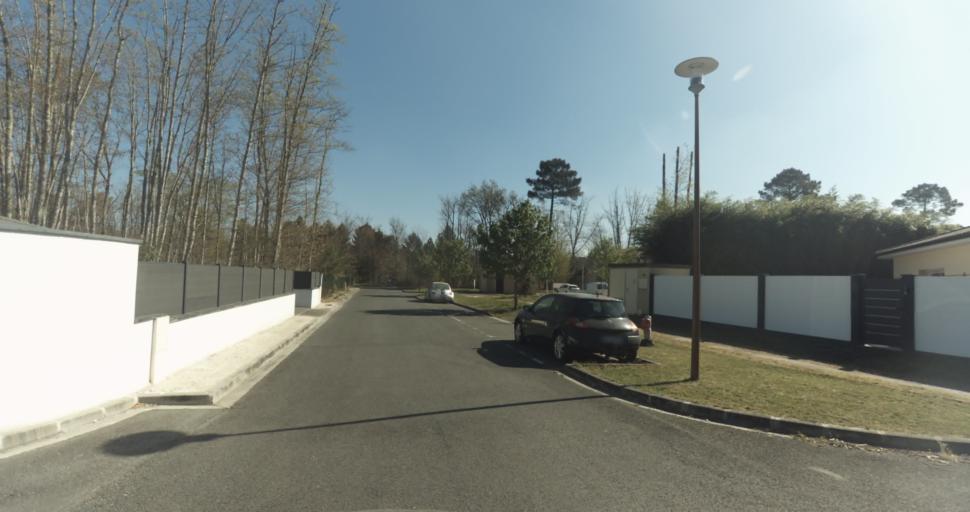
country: FR
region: Aquitaine
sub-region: Departement de la Gironde
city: Martignas-sur-Jalle
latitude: 44.7967
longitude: -0.8357
